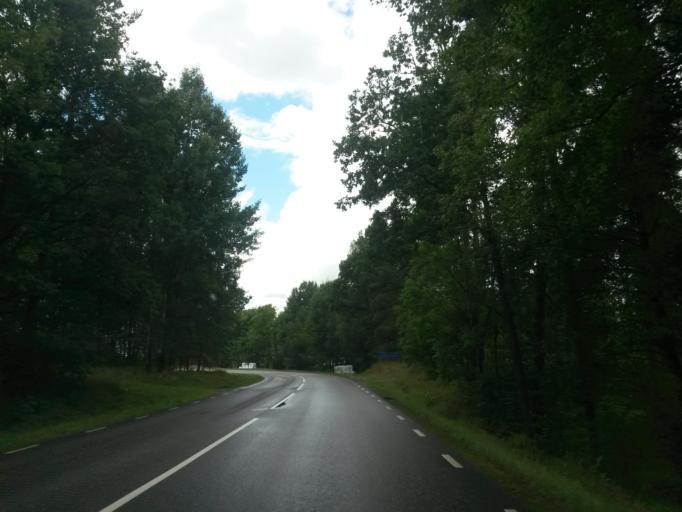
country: SE
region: Vaestra Goetaland
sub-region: Herrljunga Kommun
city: Herrljunga
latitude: 57.9953
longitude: 12.9521
